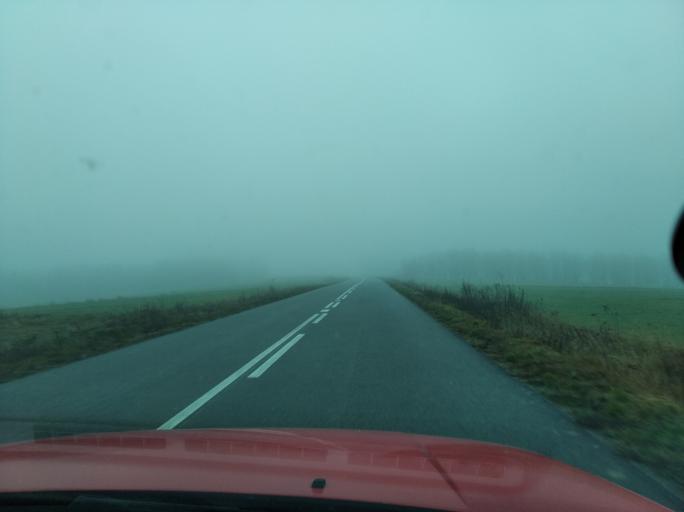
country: PL
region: Subcarpathian Voivodeship
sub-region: Powiat jaroslawski
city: Jodlowka
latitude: 49.8826
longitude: 22.4577
